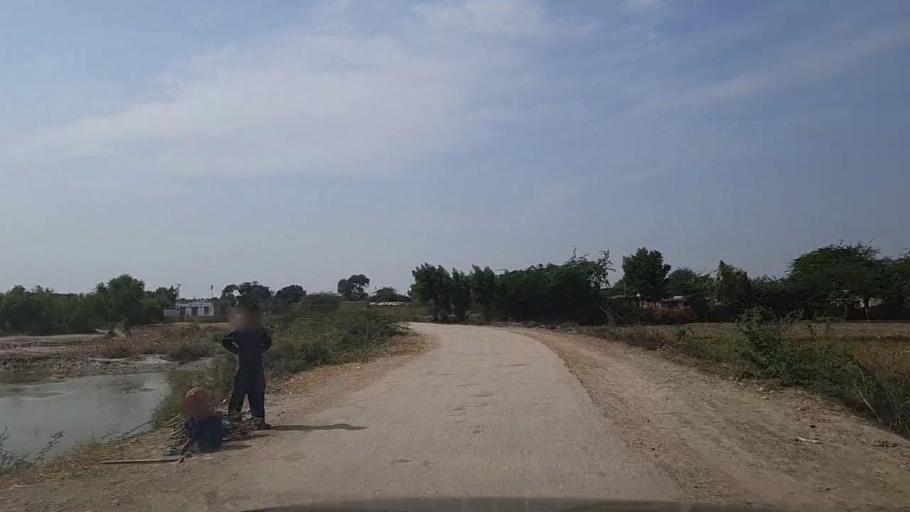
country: PK
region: Sindh
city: Thatta
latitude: 24.7833
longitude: 67.8314
